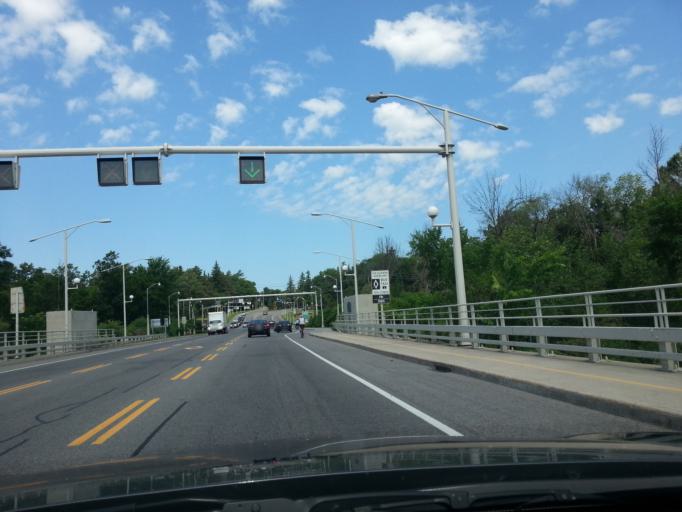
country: CA
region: Ontario
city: Ottawa
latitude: 45.4119
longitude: -75.7631
